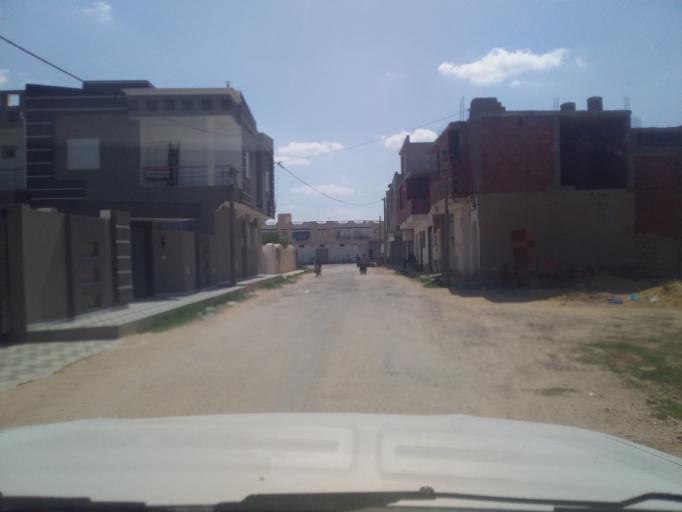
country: TN
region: Qabis
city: Matmata
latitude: 33.6150
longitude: 10.2932
